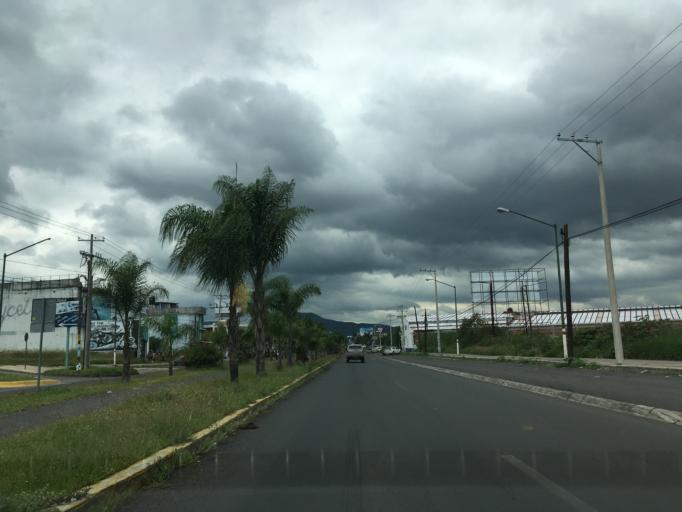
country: MX
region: Guanajuato
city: Moroleon
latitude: 20.1098
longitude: -101.1705
